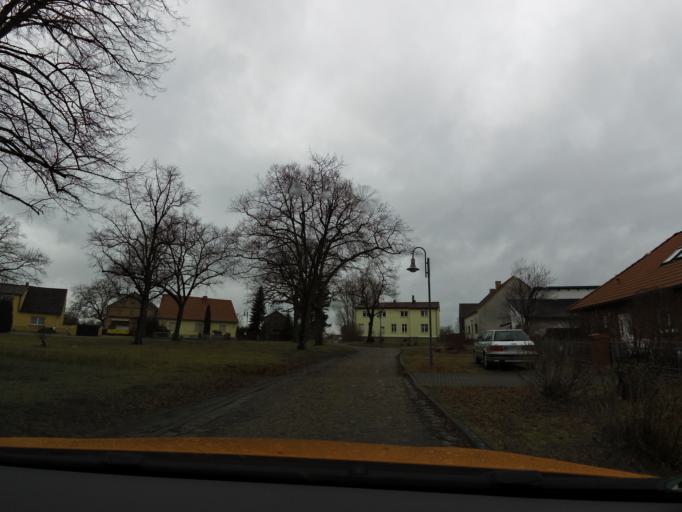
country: DE
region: Brandenburg
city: Sperenberg
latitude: 52.1678
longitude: 13.3610
